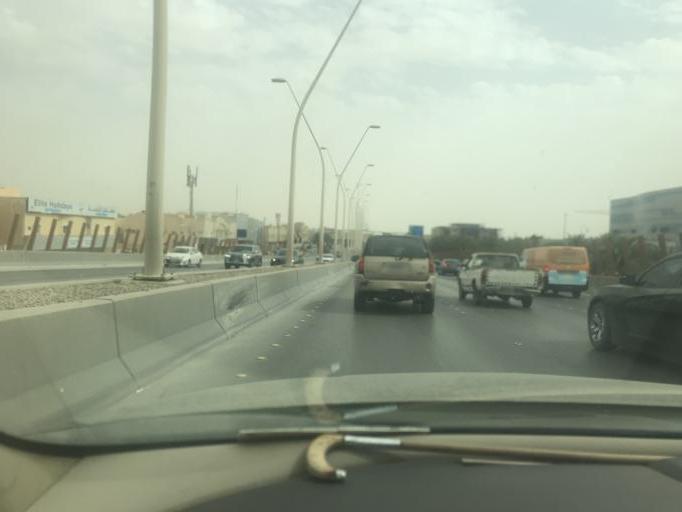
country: SA
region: Ar Riyad
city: Riyadh
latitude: 24.7420
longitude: 46.7042
